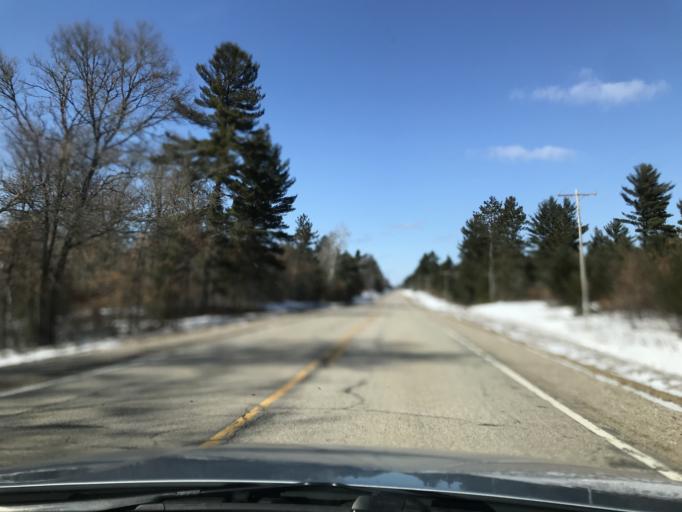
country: US
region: Wisconsin
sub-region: Marinette County
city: Niagara
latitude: 45.3848
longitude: -88.0996
